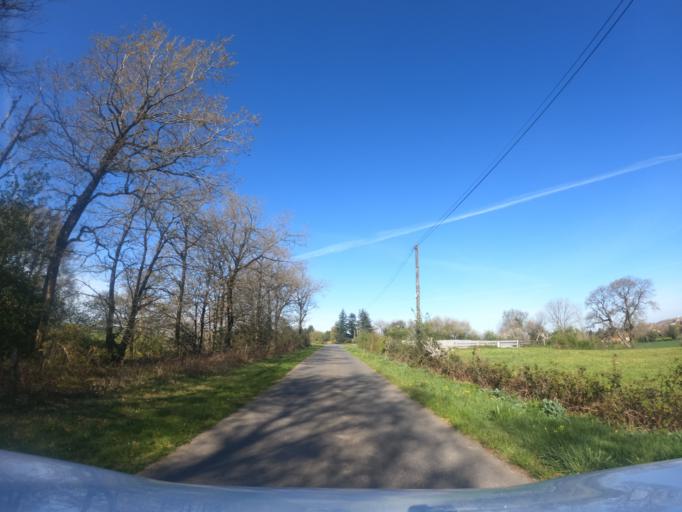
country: FR
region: Pays de la Loire
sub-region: Departement de la Vendee
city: Saint-Pierre-du-Chemin
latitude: 46.6889
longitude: -0.7006
